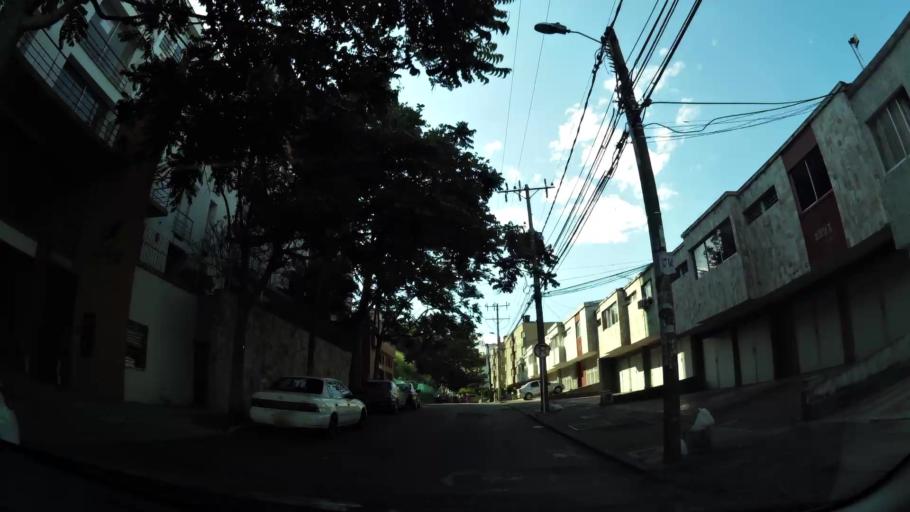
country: CO
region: Valle del Cauca
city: Cali
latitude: 3.4422
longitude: -76.5462
